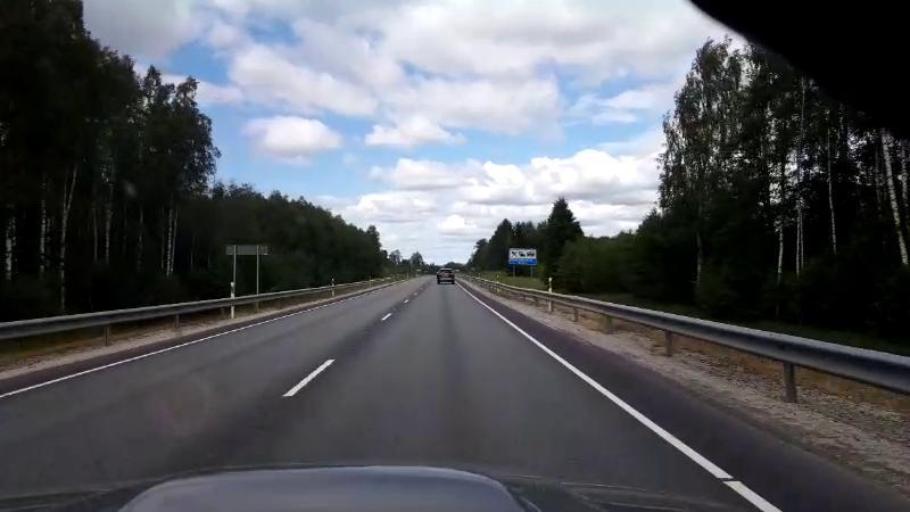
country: EE
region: Harju
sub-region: Nissi vald
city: Riisipere
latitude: 59.0713
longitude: 24.4522
